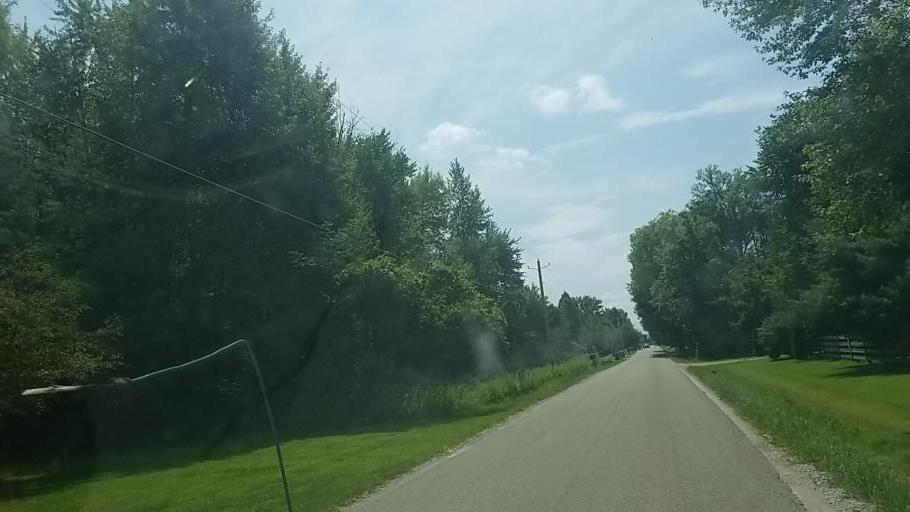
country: US
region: Ohio
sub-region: Franklin County
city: New Albany
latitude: 40.0348
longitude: -82.7688
